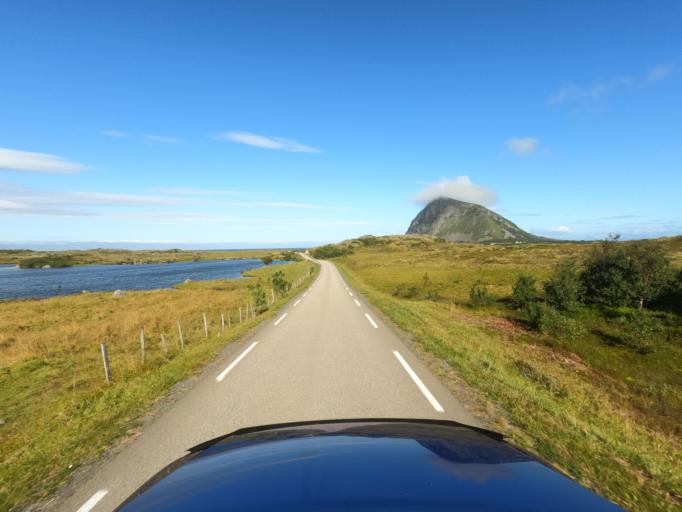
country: NO
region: Nordland
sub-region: Vestvagoy
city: Evjen
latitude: 68.3089
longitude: 14.0972
